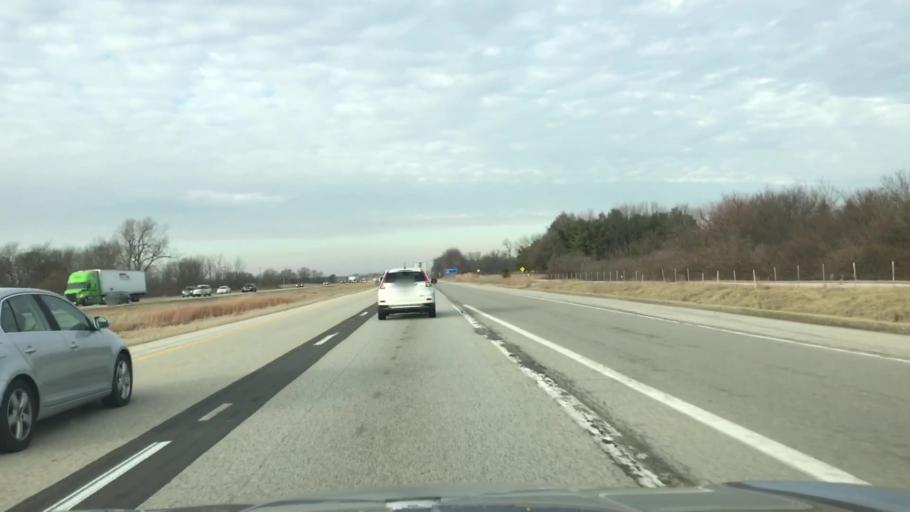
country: US
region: Illinois
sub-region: Sangamon County
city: Divernon
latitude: 39.5722
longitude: -89.6461
